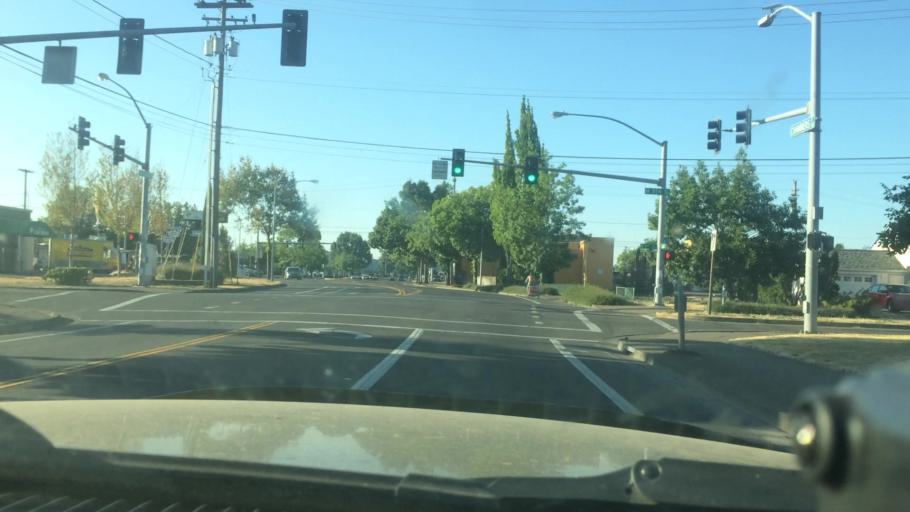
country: US
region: Oregon
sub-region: Lane County
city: Eugene
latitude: 44.0506
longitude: -123.1180
